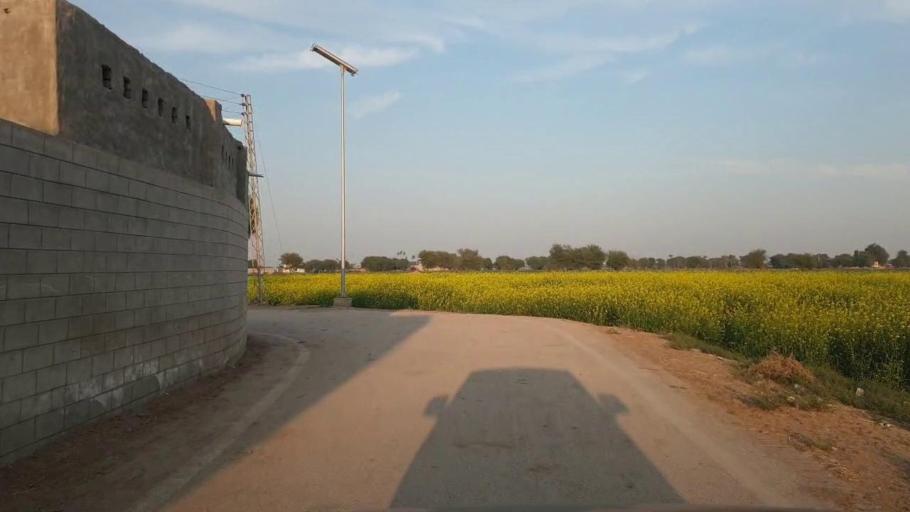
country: PK
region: Sindh
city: Shahpur Chakar
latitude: 26.1702
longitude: 68.6197
